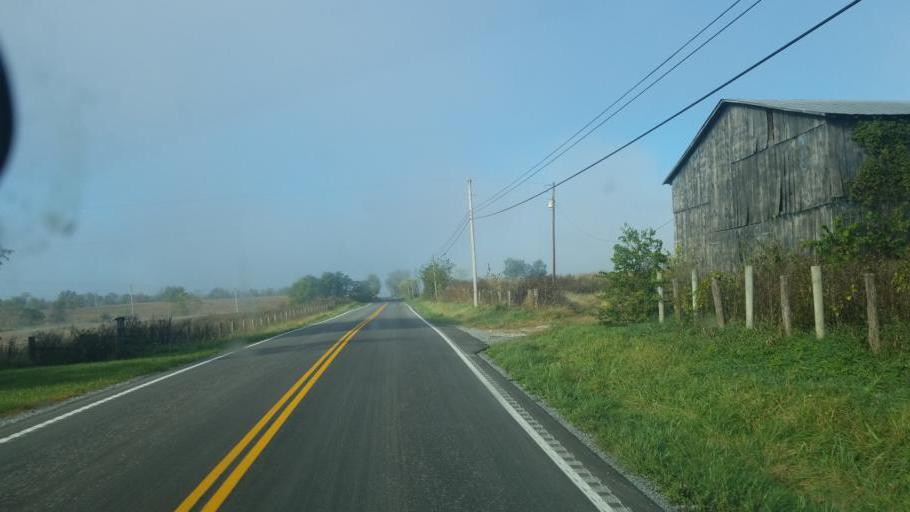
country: US
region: Kentucky
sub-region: Fleming County
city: Flemingsburg
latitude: 38.4788
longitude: -83.6549
